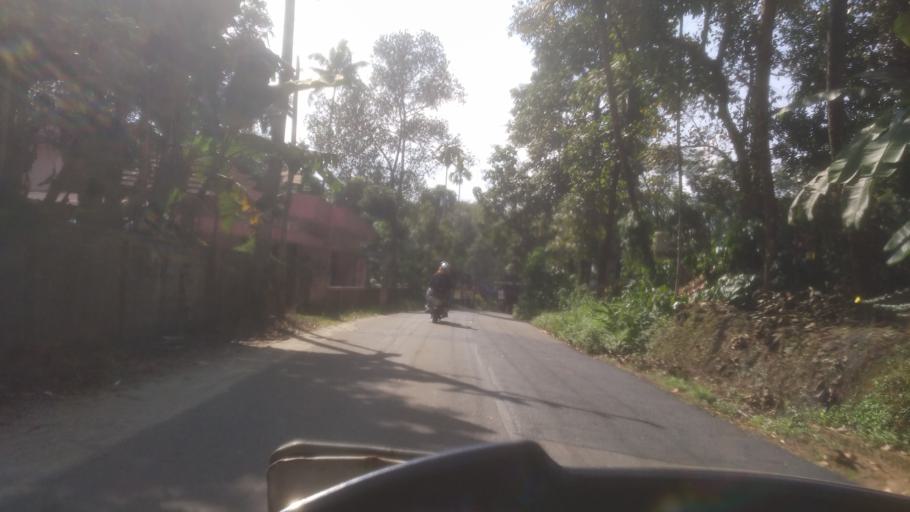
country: IN
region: Kerala
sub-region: Ernakulam
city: Kotamangalam
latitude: 10.0022
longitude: 76.7224
